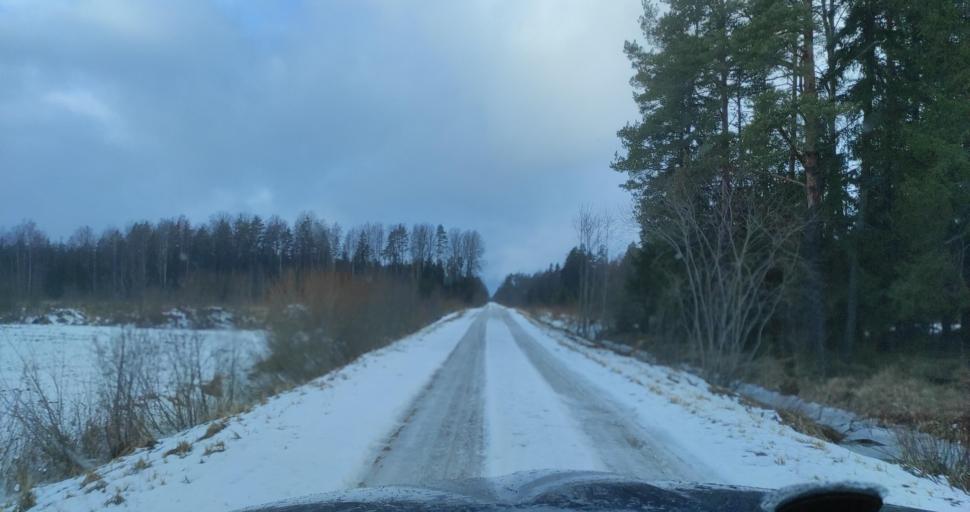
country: LV
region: Dundaga
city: Dundaga
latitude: 57.4035
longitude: 22.1000
